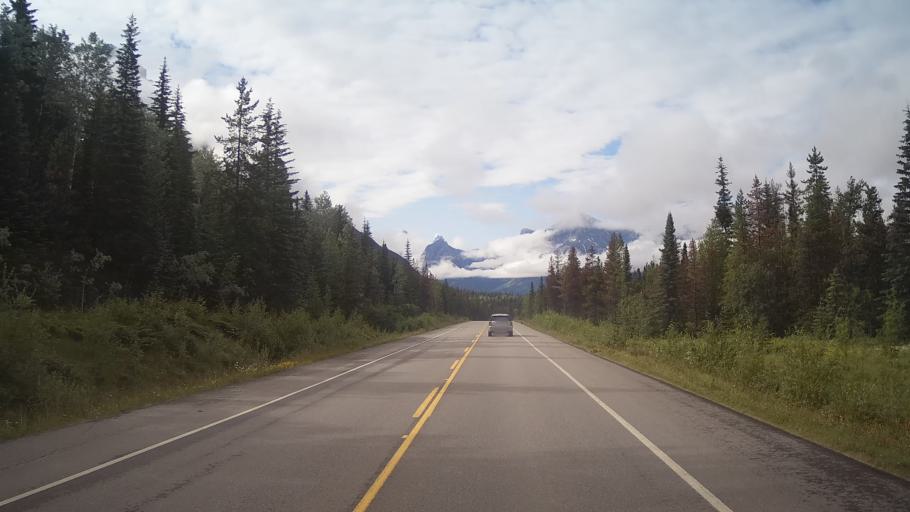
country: CA
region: Alberta
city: Jasper Park Lodge
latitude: 52.6898
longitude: -117.8658
